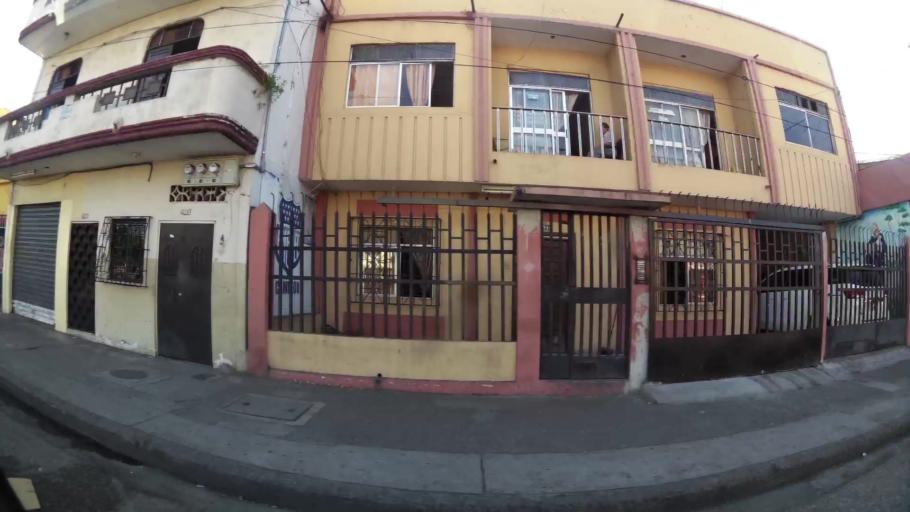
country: EC
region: Guayas
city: Guayaquil
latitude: -2.2019
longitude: -79.9165
